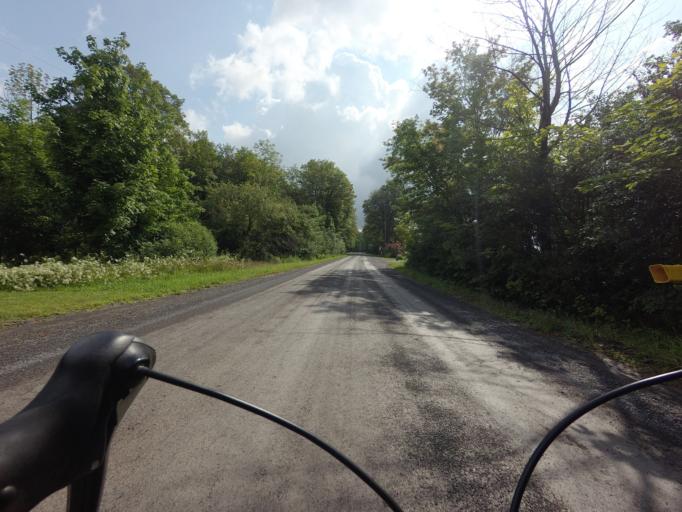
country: CA
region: Ontario
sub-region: Lanark County
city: Smiths Falls
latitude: 44.9261
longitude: -75.7497
